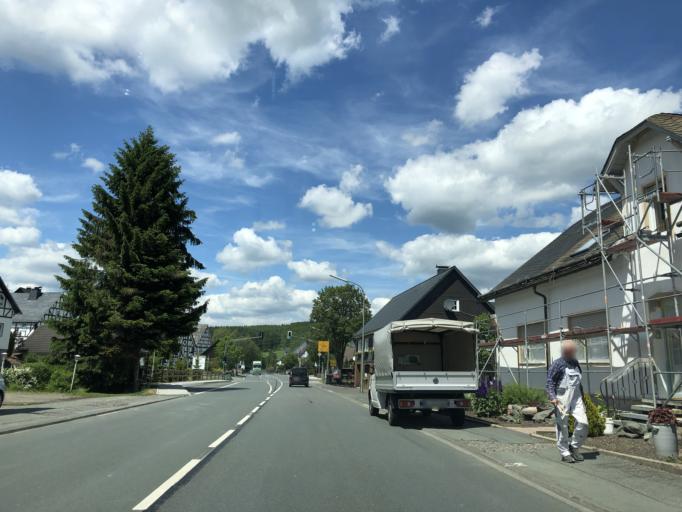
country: DE
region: North Rhine-Westphalia
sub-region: Regierungsbezirk Arnsberg
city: Erndtebruck
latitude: 50.9979
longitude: 8.2955
